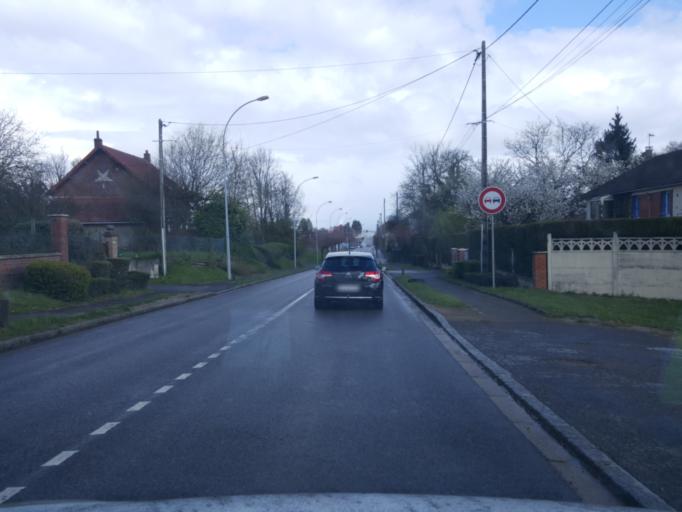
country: FR
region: Picardie
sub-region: Departement de l'Oise
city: Auneuil
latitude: 49.3690
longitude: 1.9866
